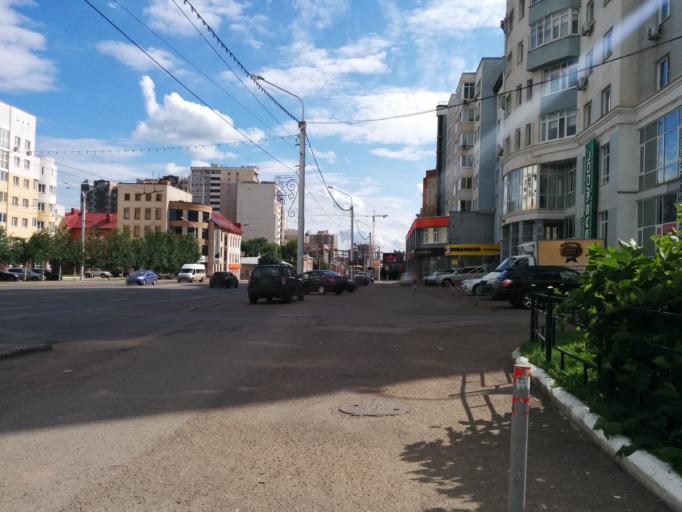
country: RU
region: Bashkortostan
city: Ufa
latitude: 54.7290
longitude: 55.9550
